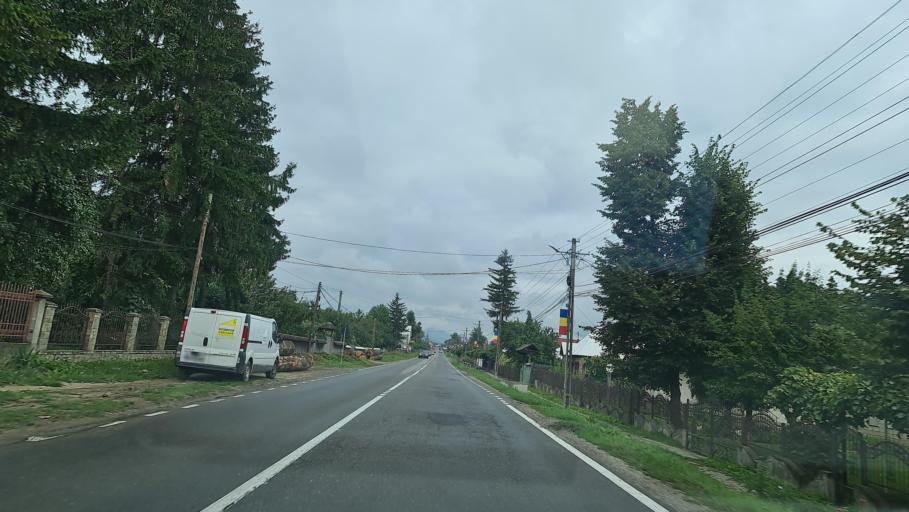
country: RO
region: Neamt
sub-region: Comuna Borlesti
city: Ruseni
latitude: 46.7988
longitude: 26.5373
